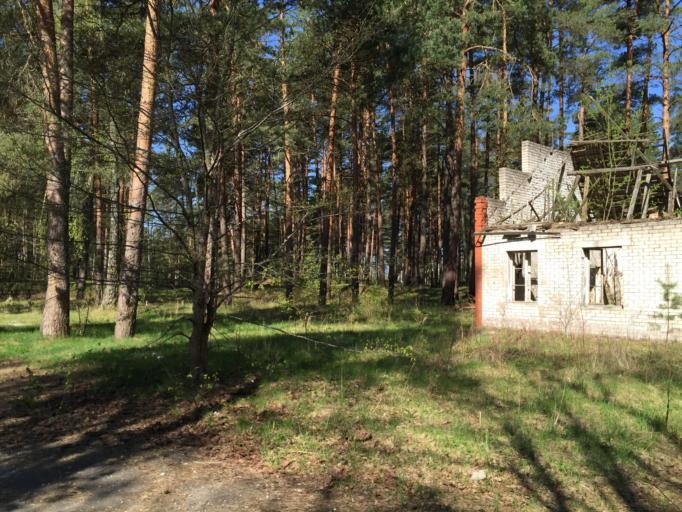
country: LV
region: Adazi
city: Adazi
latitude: 57.0915
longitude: 24.3416
